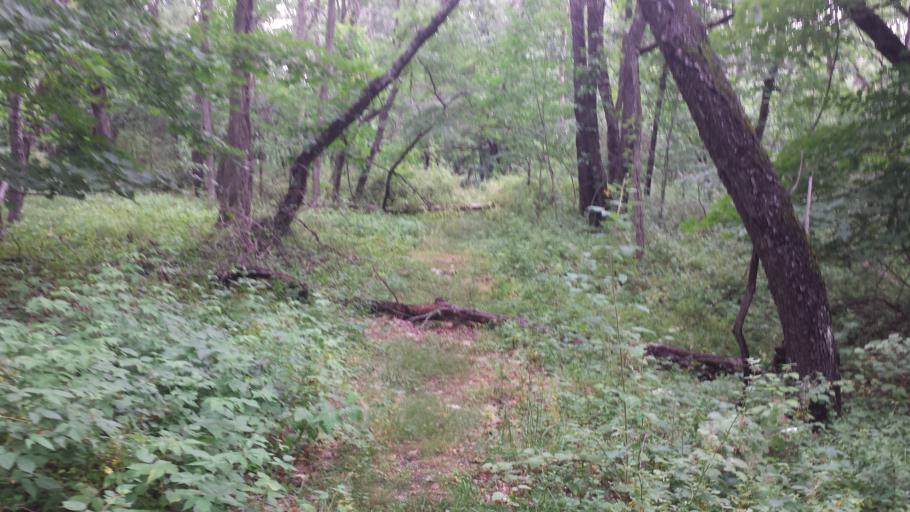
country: US
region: New York
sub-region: Westchester County
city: Crugers
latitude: 41.2343
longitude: -73.9370
